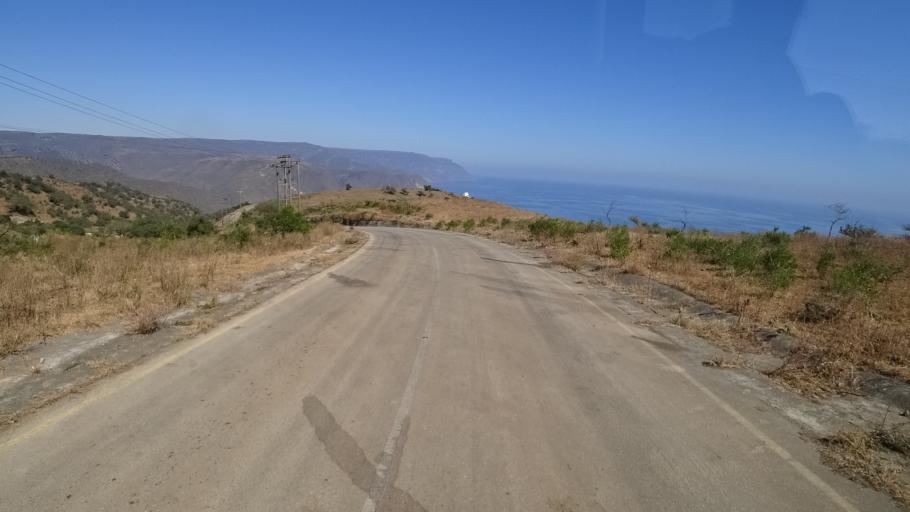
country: YE
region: Al Mahrah
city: Hawf
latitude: 16.7411
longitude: 53.3667
